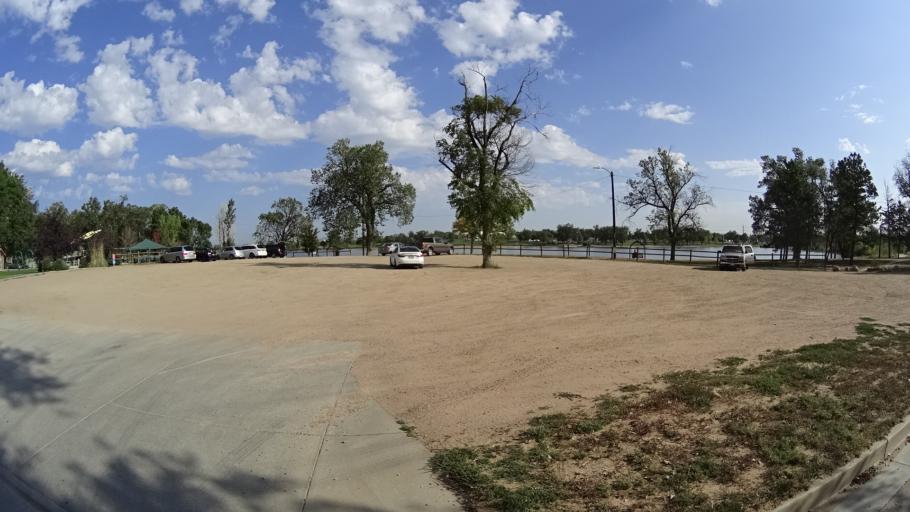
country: US
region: Colorado
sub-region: El Paso County
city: Colorado Springs
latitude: 38.8222
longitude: -104.7987
